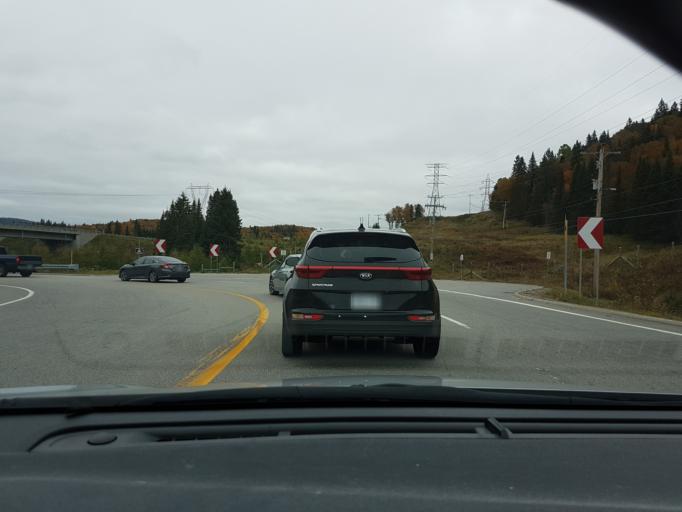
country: CA
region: Quebec
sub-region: Capitale-Nationale
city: Shannon
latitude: 47.1066
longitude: -71.3433
